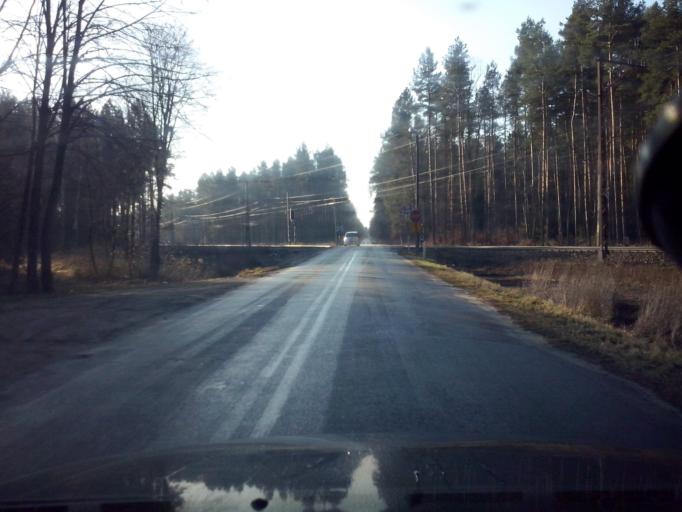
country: PL
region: Subcarpathian Voivodeship
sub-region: Powiat lezajski
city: Letownia
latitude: 50.3736
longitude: 22.2525
